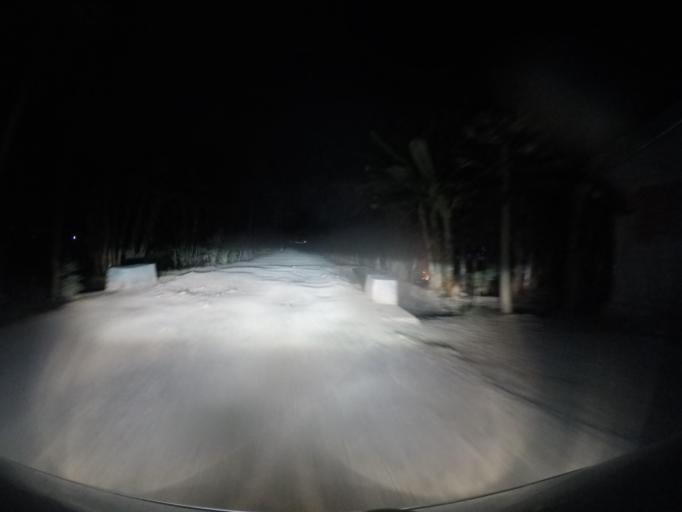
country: TL
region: Viqueque
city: Viqueque
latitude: -8.7964
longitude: 126.5565
